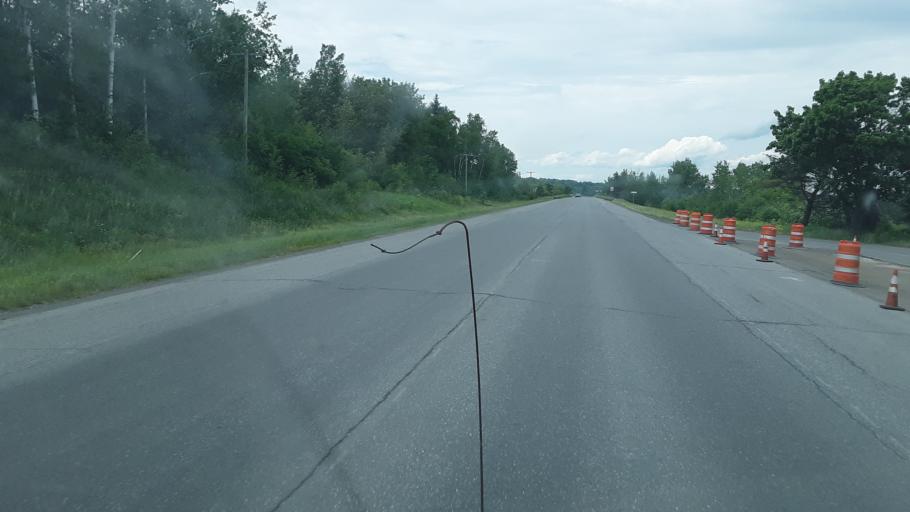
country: US
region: Maine
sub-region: Aroostook County
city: Caribou
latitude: 46.8451
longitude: -68.0038
